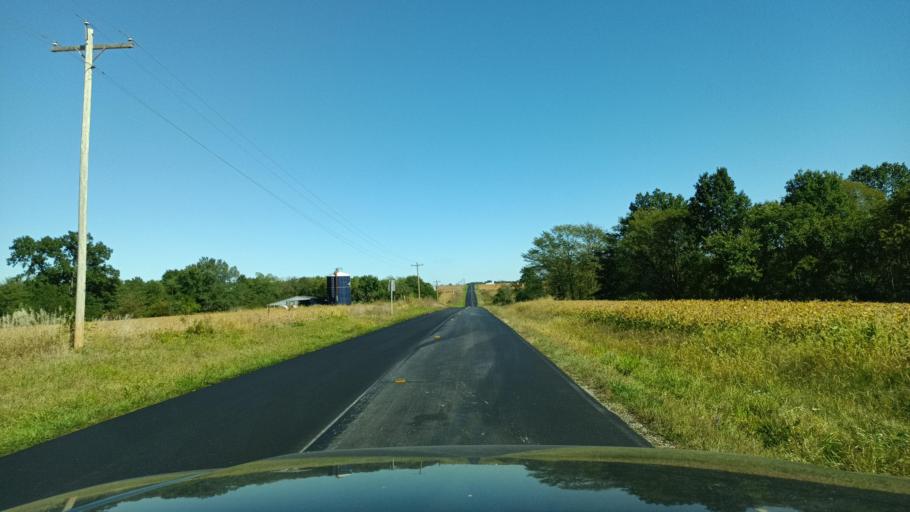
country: US
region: Missouri
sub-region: Macon County
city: La Plata
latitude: 39.9279
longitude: -92.5666
